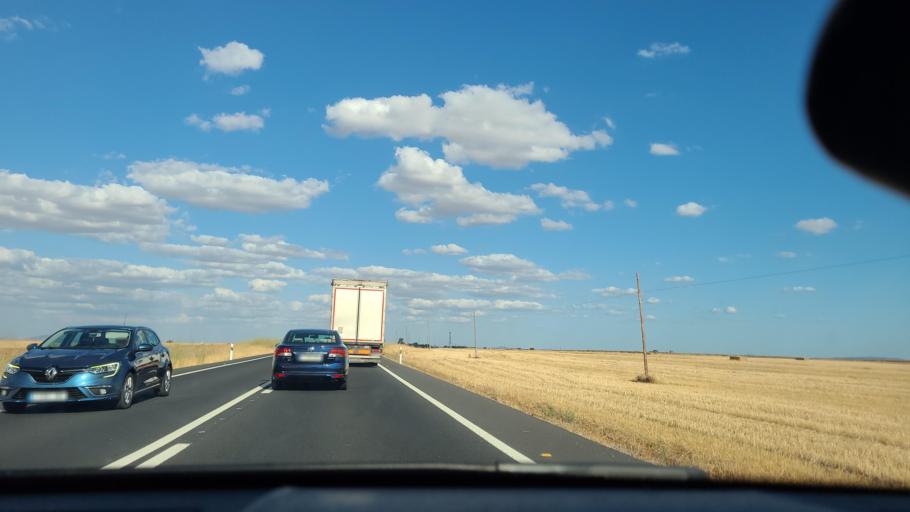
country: ES
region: Extremadura
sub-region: Provincia de Badajoz
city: Azuaga
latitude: 38.2644
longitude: -5.7431
